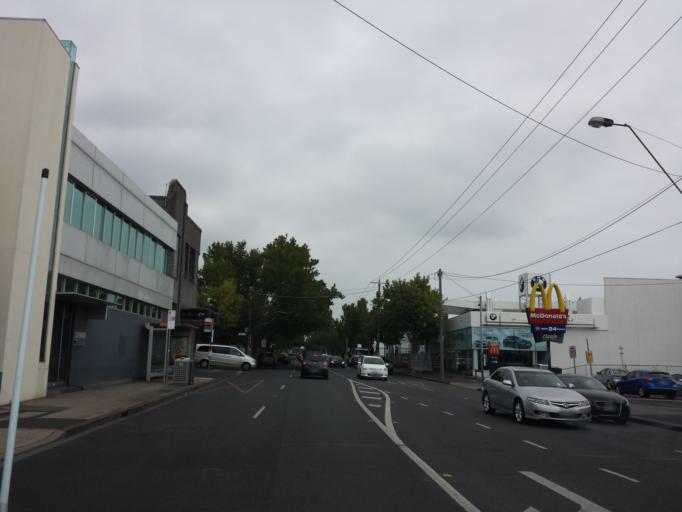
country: AU
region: Victoria
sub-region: Stonnington
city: Toorak
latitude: -37.8483
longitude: 145.0032
